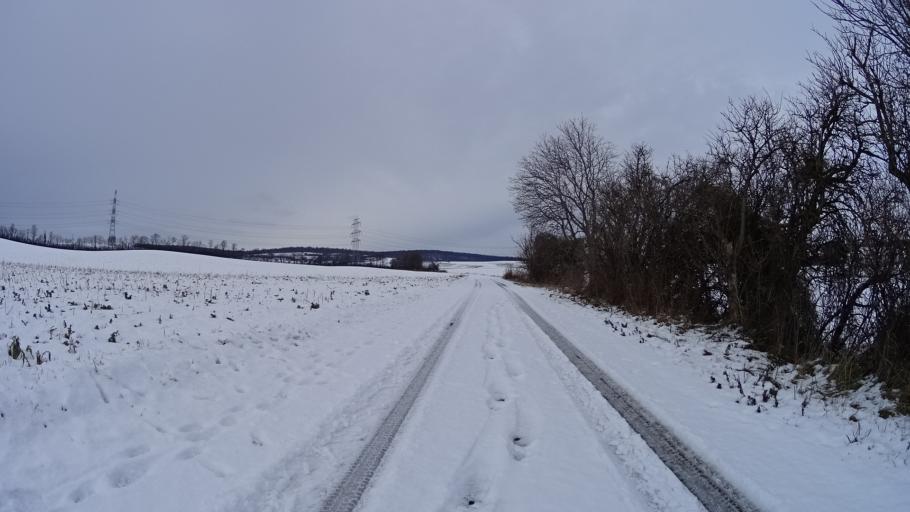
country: AT
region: Lower Austria
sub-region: Politischer Bezirk Korneuburg
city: Harmannsdorf
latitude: 48.3937
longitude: 16.3500
